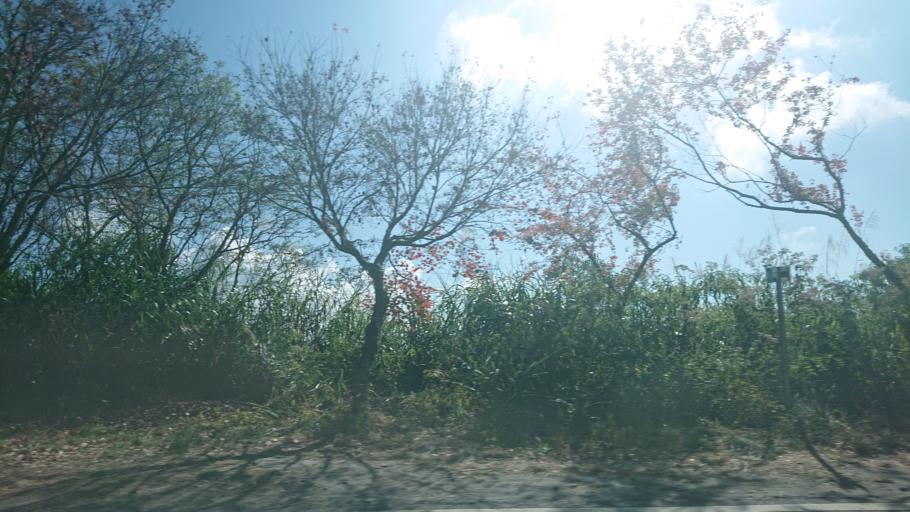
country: TW
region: Taiwan
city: Lugu
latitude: 23.5040
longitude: 120.8100
